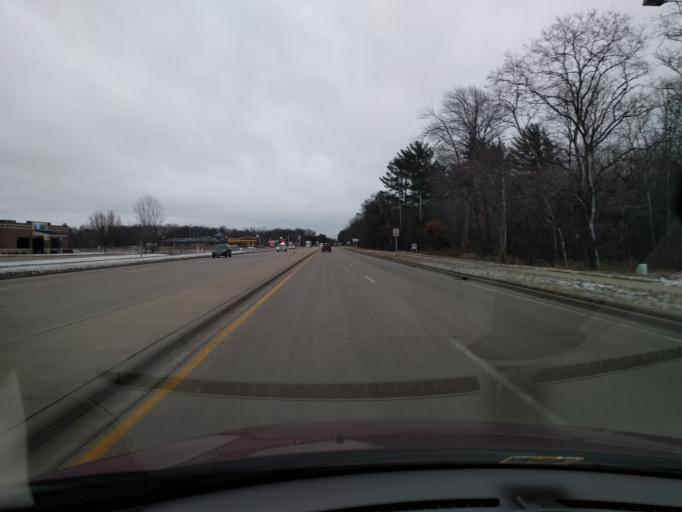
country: US
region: Wisconsin
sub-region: Portage County
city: Whiting
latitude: 44.5235
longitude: -89.5035
